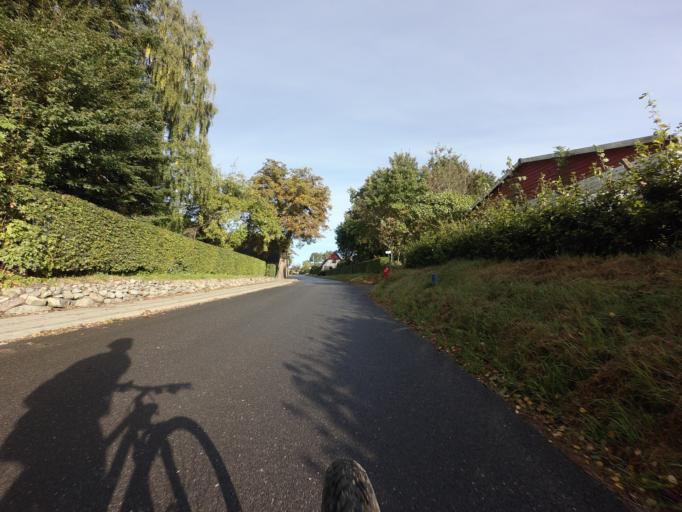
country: DK
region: Central Jutland
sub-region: Viborg Kommune
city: Bjerringbro
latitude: 56.4427
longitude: 9.5577
